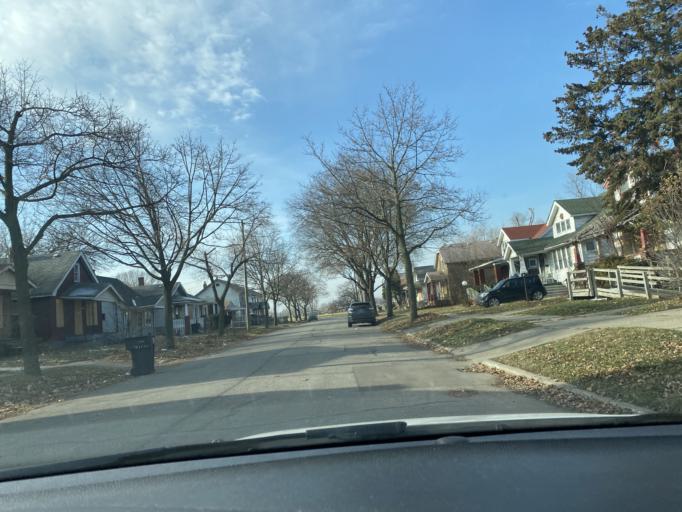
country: US
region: Michigan
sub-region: Wayne County
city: Highland Park
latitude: 42.3752
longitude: -83.1429
